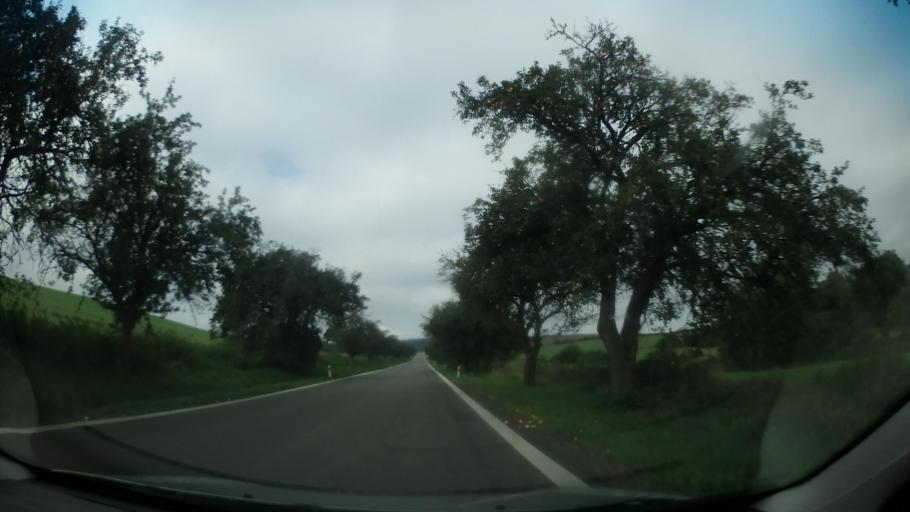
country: CZ
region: Central Bohemia
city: Neveklov
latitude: 49.7535
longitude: 14.5910
